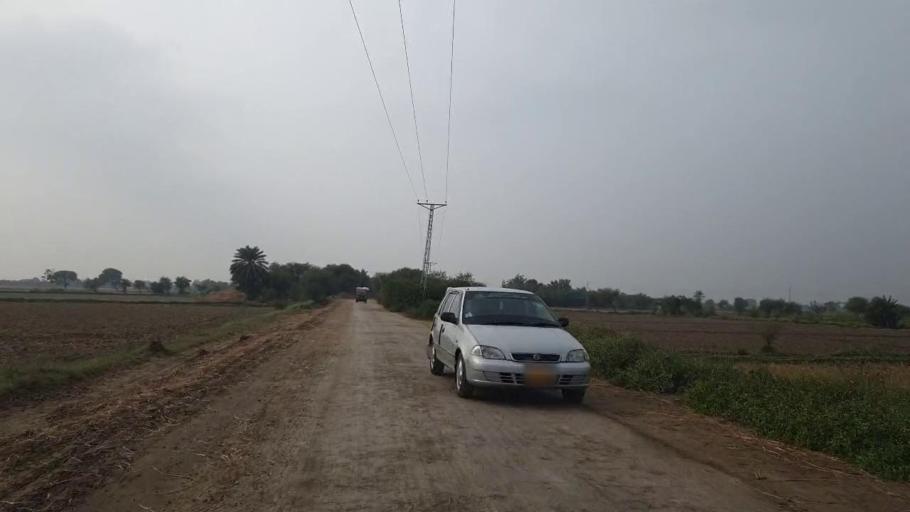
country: PK
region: Sindh
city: Matli
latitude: 24.9439
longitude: 68.5763
